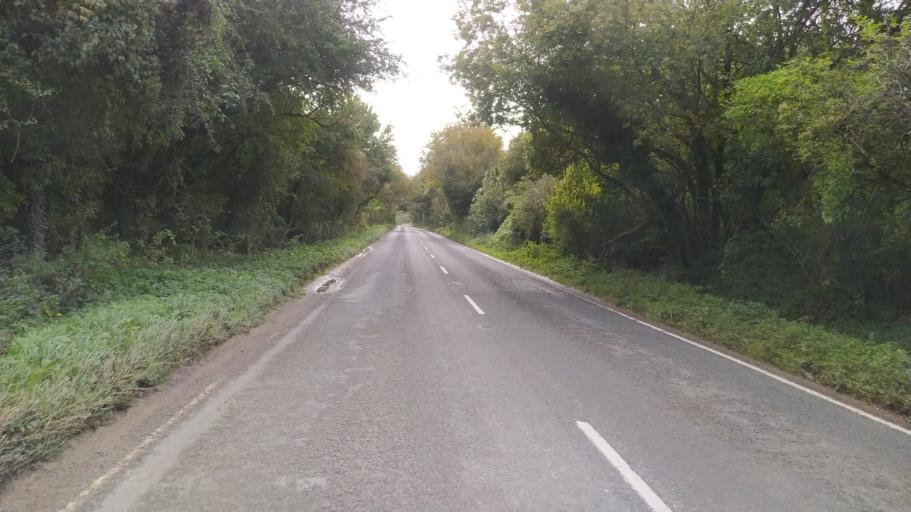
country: GB
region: England
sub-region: Hampshire
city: Romsey
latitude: 51.0441
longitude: -1.5205
